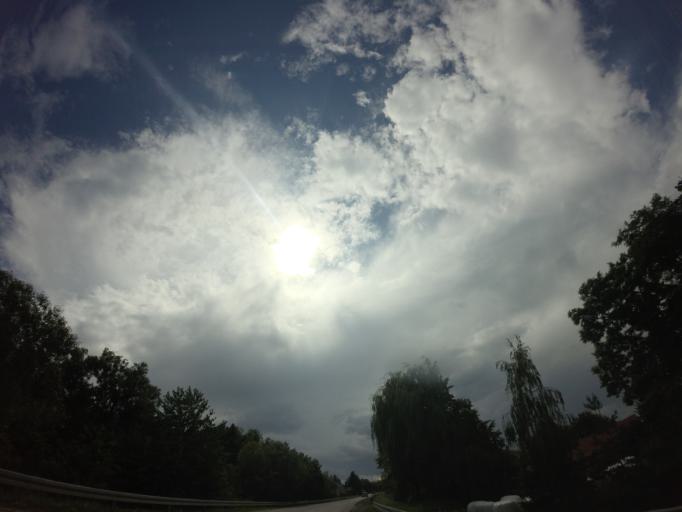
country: PL
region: Swietokrzyskie
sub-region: Powiat staszowski
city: Bogoria
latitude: 50.6977
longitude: 21.2422
